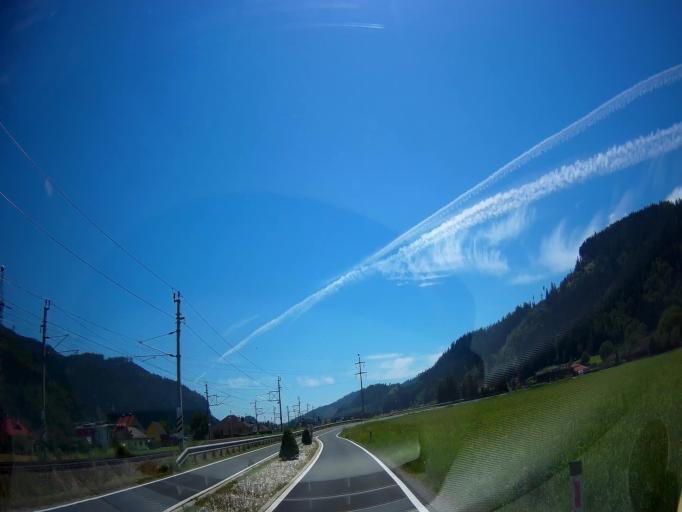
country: AT
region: Carinthia
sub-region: Politischer Bezirk Sankt Veit an der Glan
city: Micheldorf
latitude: 46.9158
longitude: 14.4308
